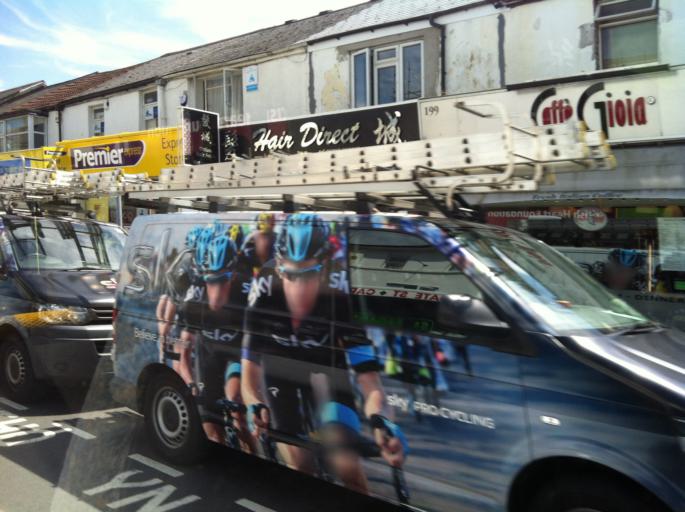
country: GB
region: Wales
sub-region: Cardiff
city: Cardiff
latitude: 51.4815
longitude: -3.1983
